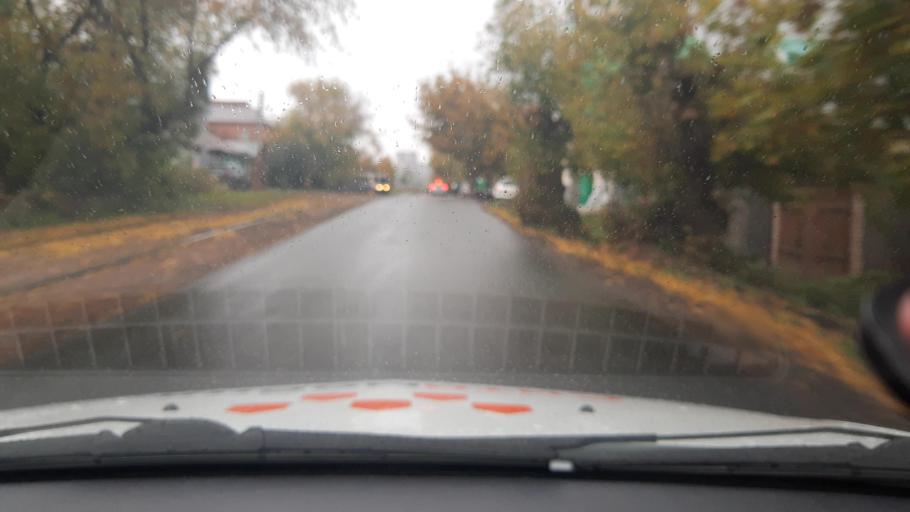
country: RU
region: Bashkortostan
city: Ufa
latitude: 54.7171
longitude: 55.9717
